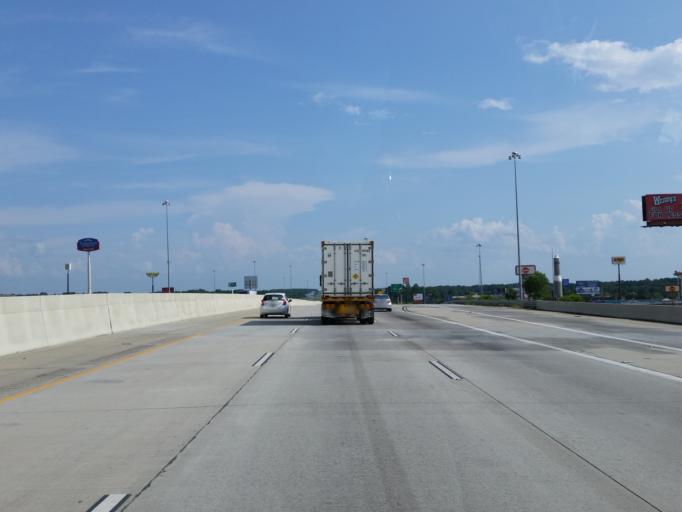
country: US
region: Georgia
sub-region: Crisp County
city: Cordele
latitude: 31.9635
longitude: -83.7522
